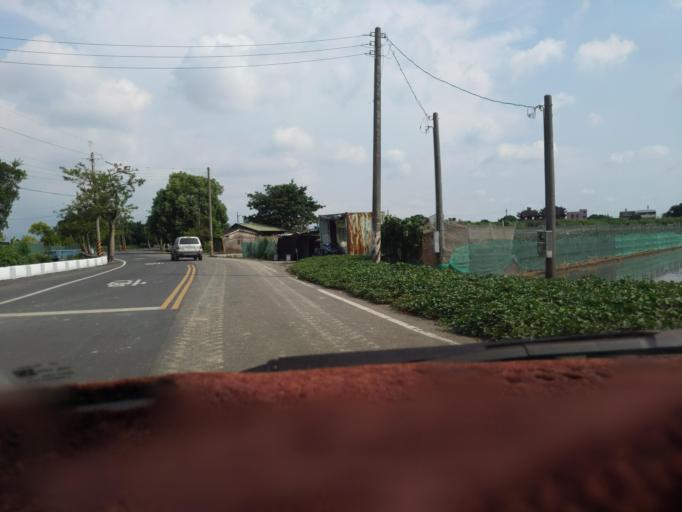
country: TW
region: Taiwan
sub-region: Yunlin
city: Douliu
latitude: 23.7899
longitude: 120.3995
